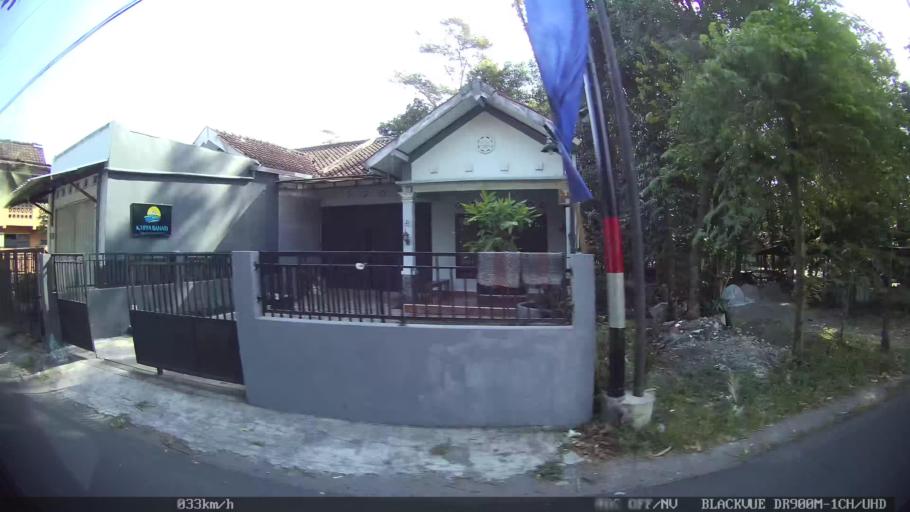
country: ID
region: Daerah Istimewa Yogyakarta
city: Kasihan
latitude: -7.8308
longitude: 110.3384
